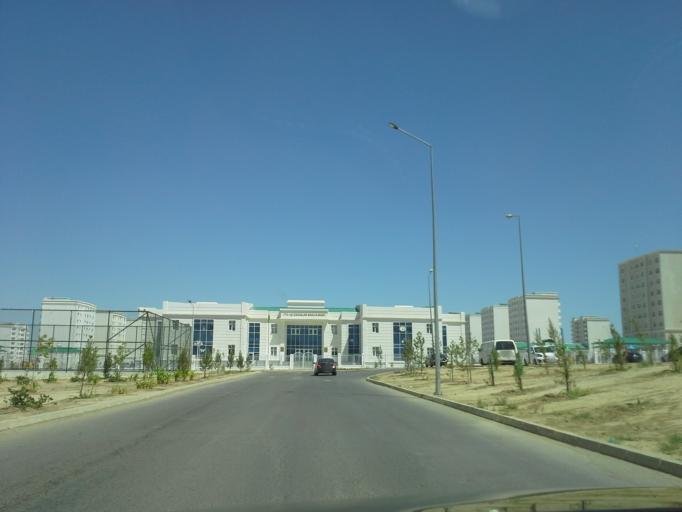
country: TM
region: Ahal
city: Ashgabat
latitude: 37.8877
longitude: 58.4064
